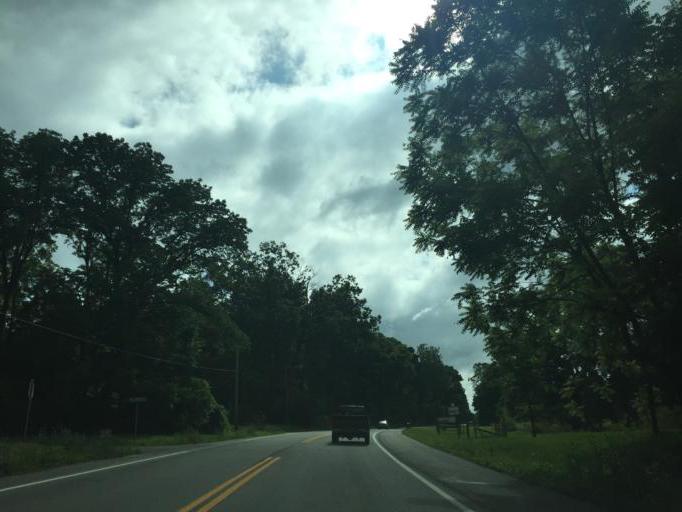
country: US
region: Maryland
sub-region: Cecil County
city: Rising Sun
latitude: 39.6949
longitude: -76.1212
